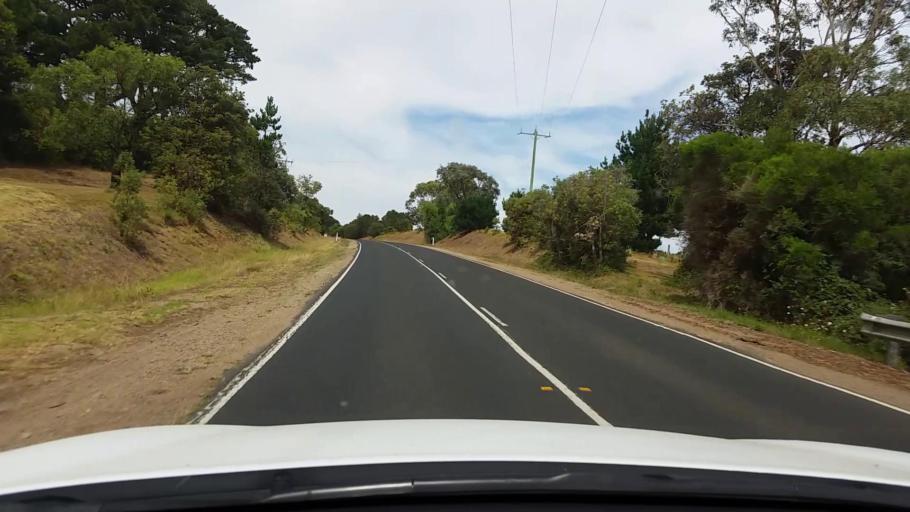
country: AU
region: Victoria
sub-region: Mornington Peninsula
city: Merricks
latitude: -38.4389
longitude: 145.0371
